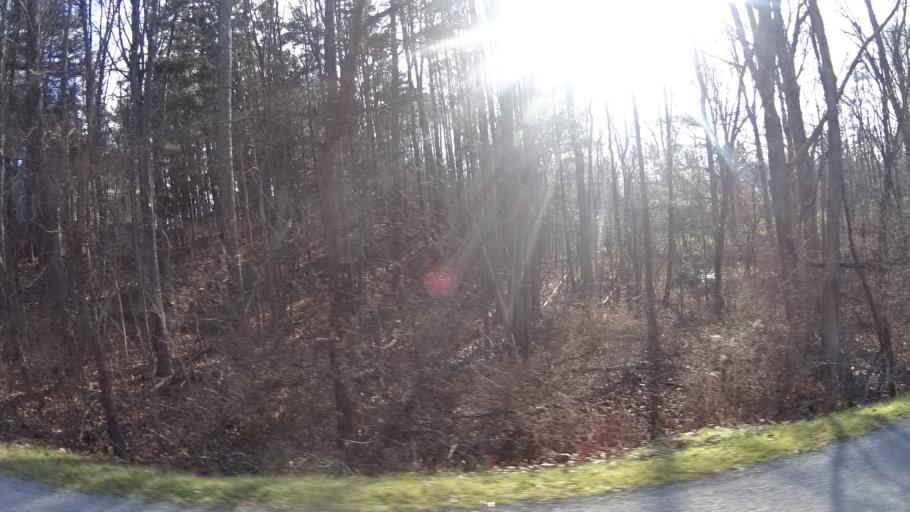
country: US
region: Ohio
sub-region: Lorain County
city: Wellington
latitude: 41.1853
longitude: -82.2714
